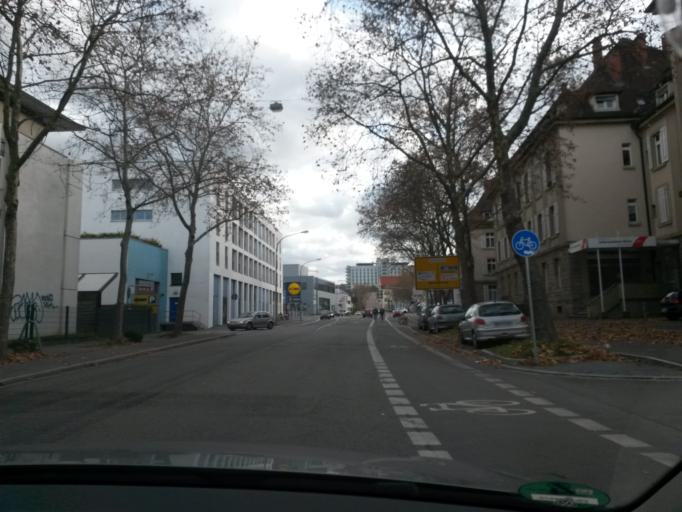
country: DE
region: Baden-Wuerttemberg
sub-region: Freiburg Region
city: Freiburg
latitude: 48.0108
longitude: 7.8307
